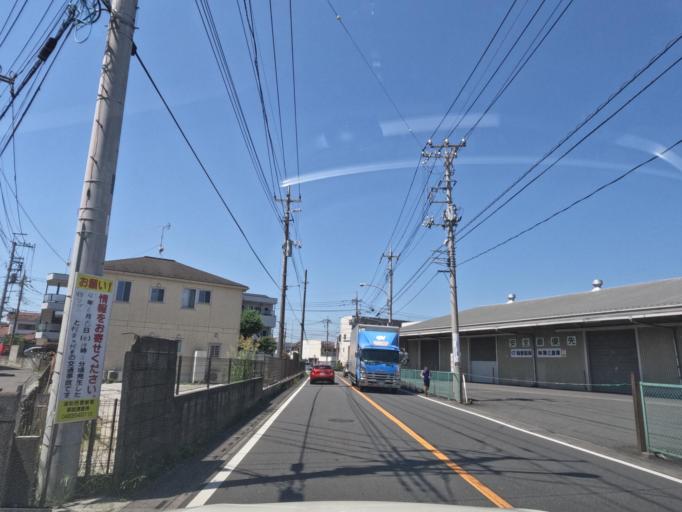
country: JP
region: Saitama
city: Yono
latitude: 35.8695
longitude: 139.6106
